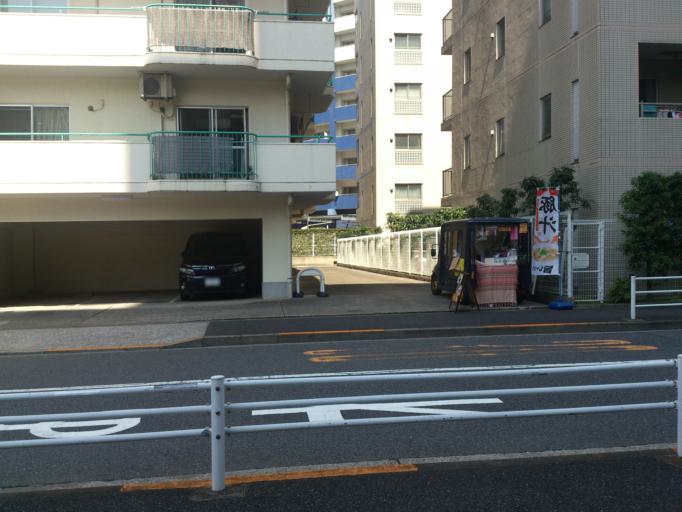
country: JP
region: Tokyo
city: Tokyo
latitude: 35.6595
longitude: 139.7738
